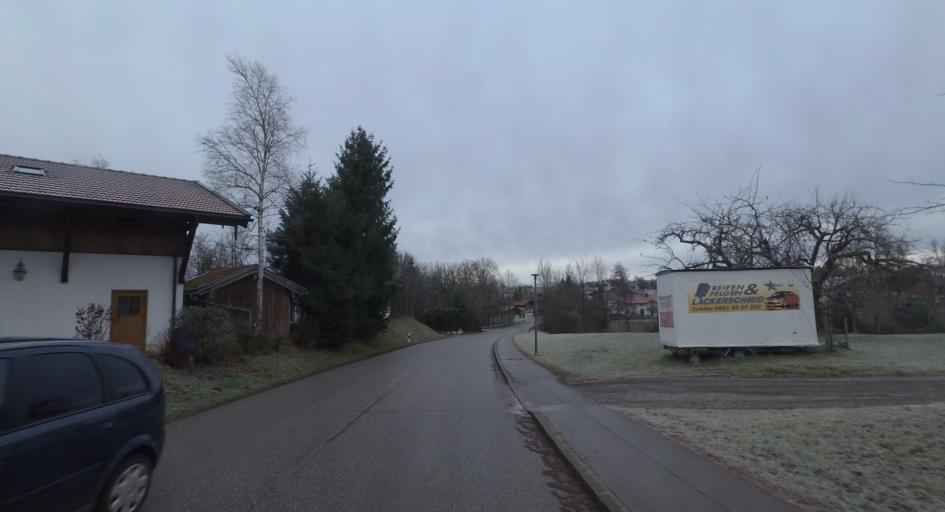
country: DE
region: Bavaria
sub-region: Upper Bavaria
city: Traunstein
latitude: 47.9143
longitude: 12.6492
